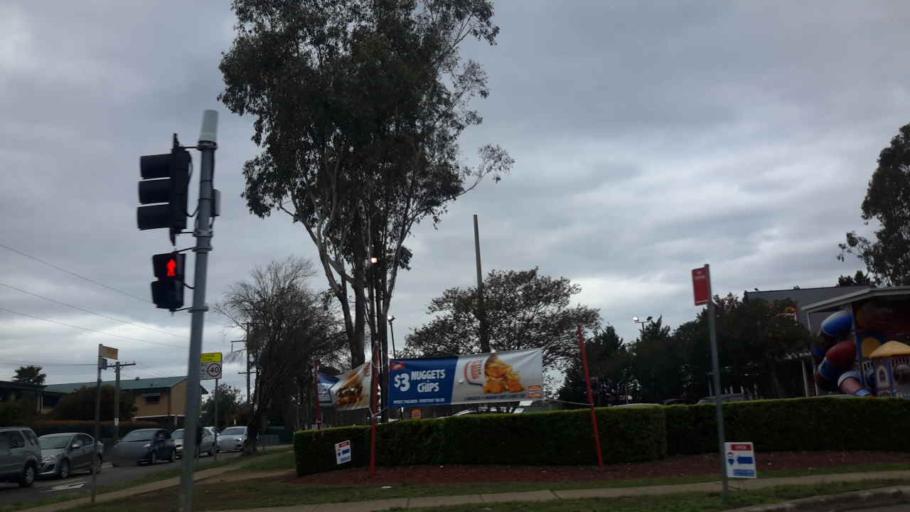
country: AU
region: New South Wales
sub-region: Penrith Municipality
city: Cambridge Park
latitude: -33.7544
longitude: 150.7128
